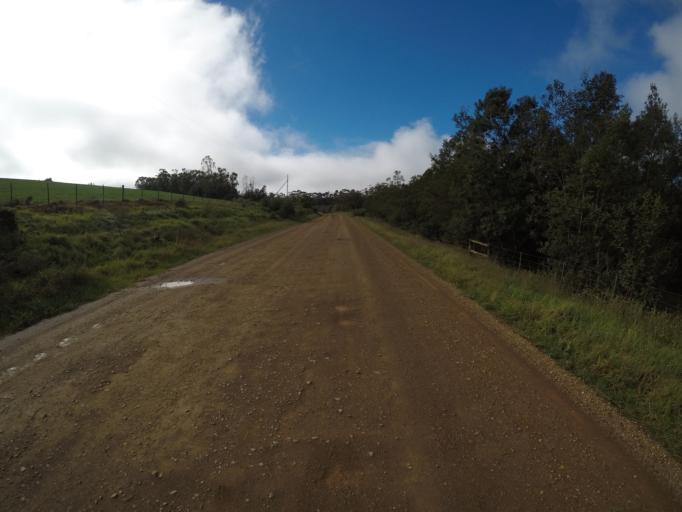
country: ZA
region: Western Cape
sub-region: Cape Winelands District Municipality
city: Ashton
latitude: -34.1126
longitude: 19.7938
